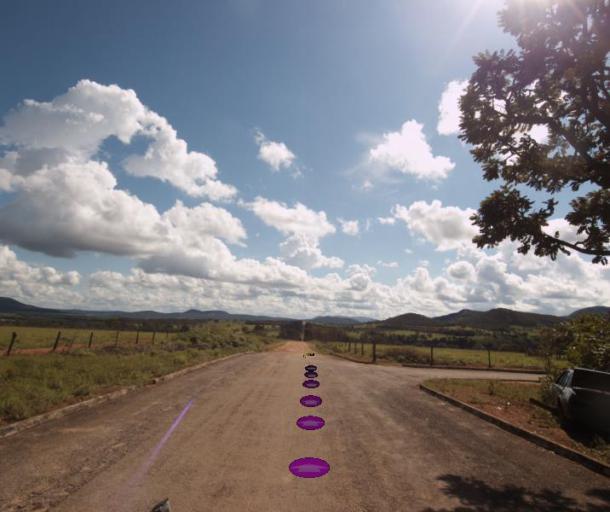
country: BR
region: Goias
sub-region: Pirenopolis
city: Pirenopolis
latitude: -15.8287
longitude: -49.1362
